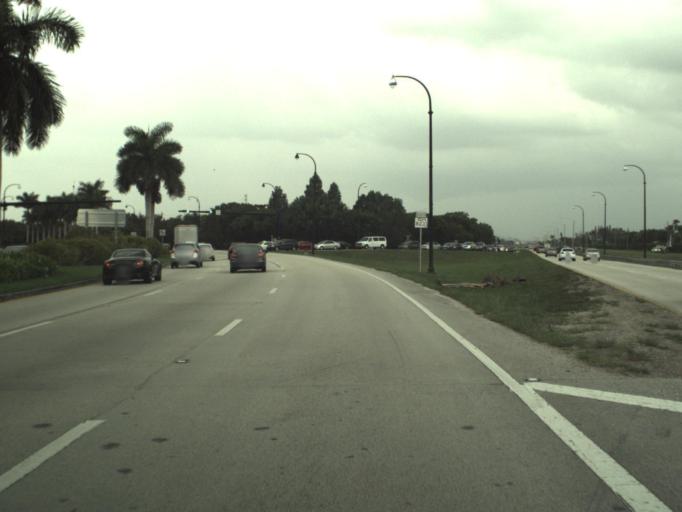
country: US
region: Florida
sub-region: Miami-Dade County
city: Country Club
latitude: 25.9915
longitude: -80.3116
